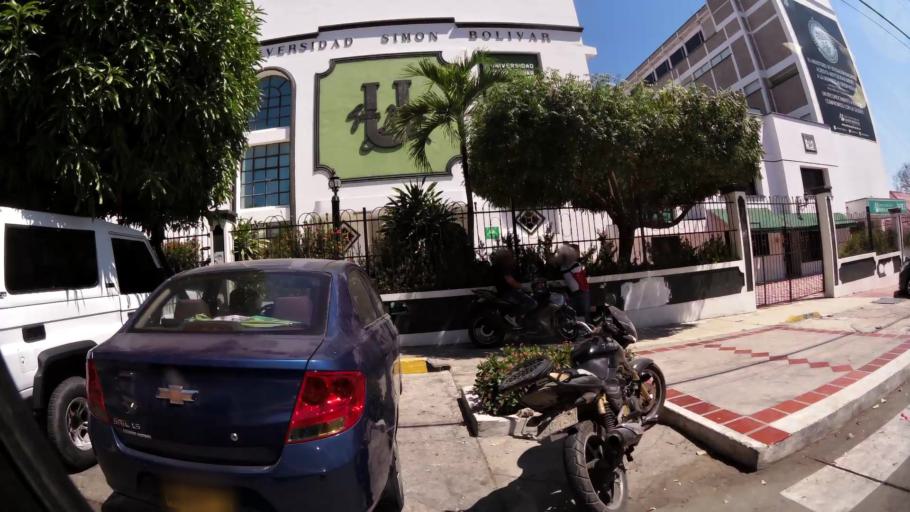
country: CO
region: Atlantico
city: Barranquilla
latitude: 10.9952
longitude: -74.7924
